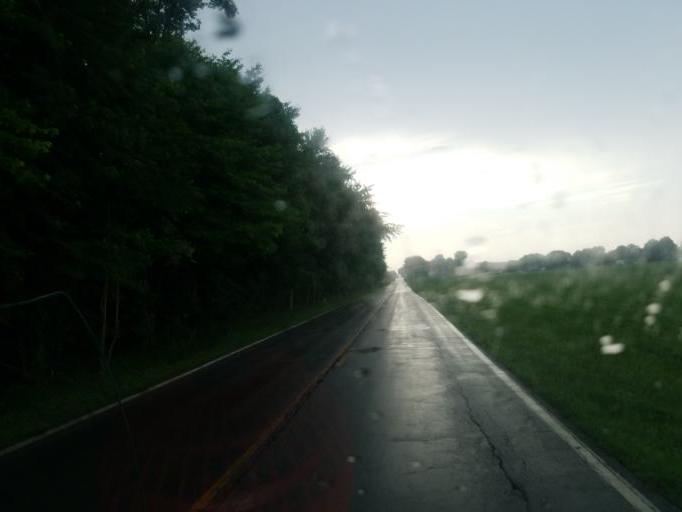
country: US
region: Ohio
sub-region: Wayne County
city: Creston
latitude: 40.9458
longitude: -81.8423
